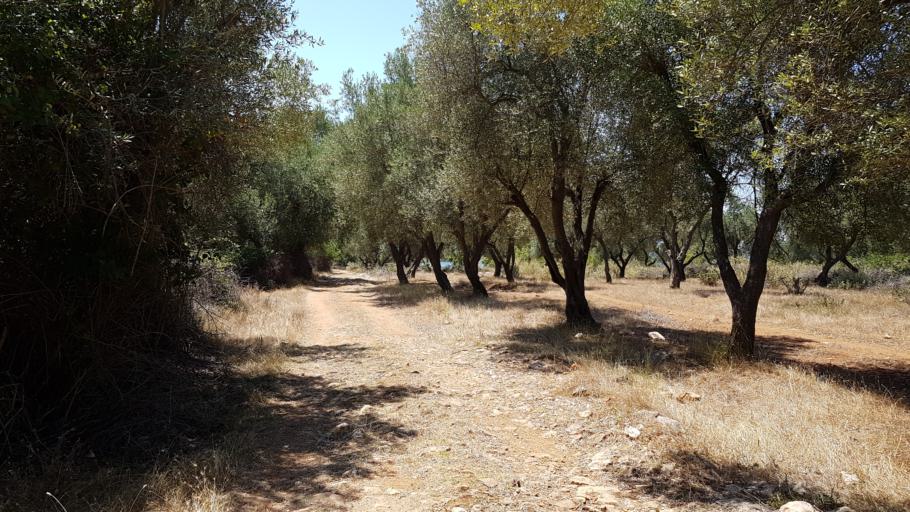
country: AL
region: Vlore
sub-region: Rrethi i Sarandes
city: Xarre
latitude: 39.7544
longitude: 20.0000
